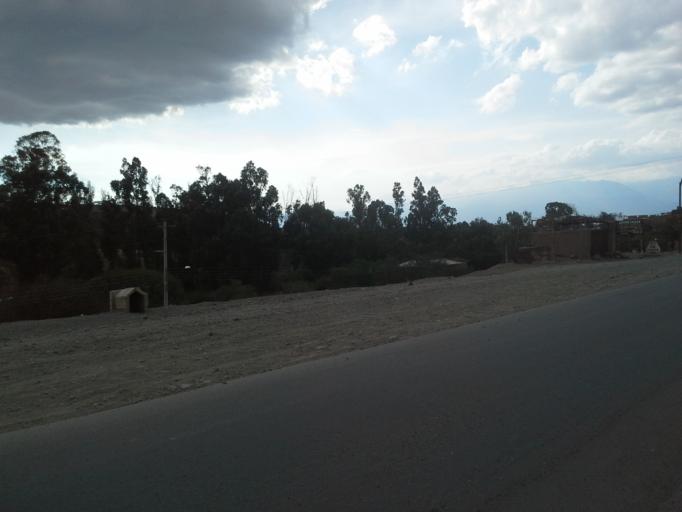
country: BO
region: Cochabamba
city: Cochabamba
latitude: -17.4692
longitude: -66.1149
